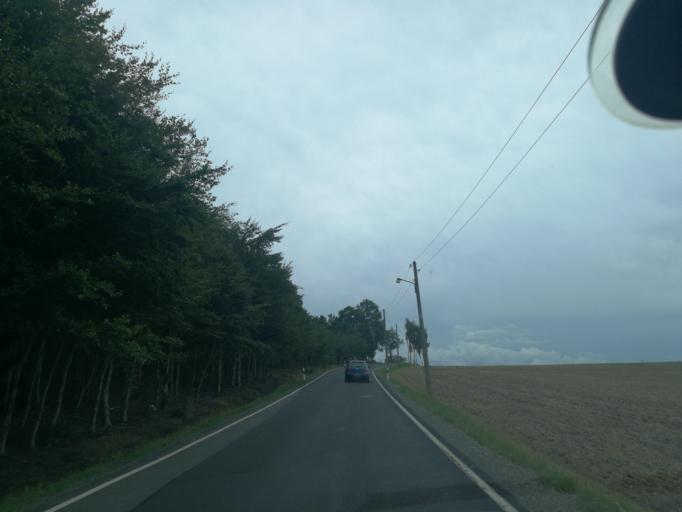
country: DE
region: Saxony
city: Triebel
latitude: 50.3347
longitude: 12.1177
